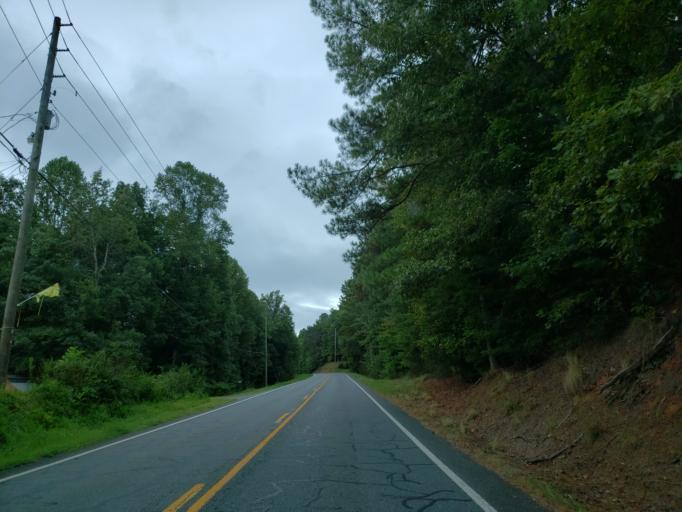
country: US
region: Georgia
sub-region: Gilmer County
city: Ellijay
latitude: 34.6344
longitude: -84.5785
